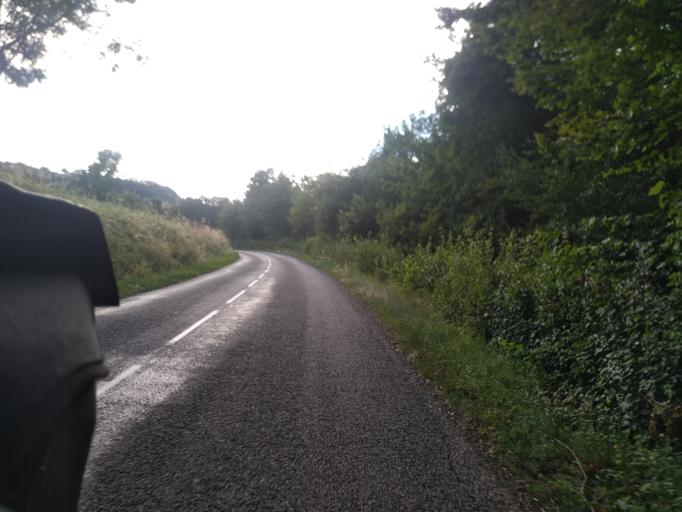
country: FR
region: Rhone-Alpes
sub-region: Departement du Rhone
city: Montrottier
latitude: 45.7889
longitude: 4.4998
